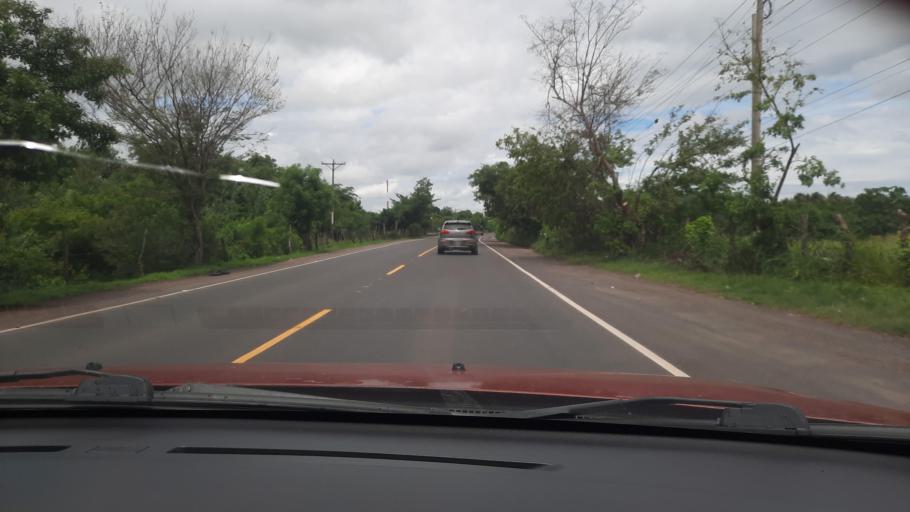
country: SV
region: Ahuachapan
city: Guaymango
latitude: 13.6992
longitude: -89.9479
